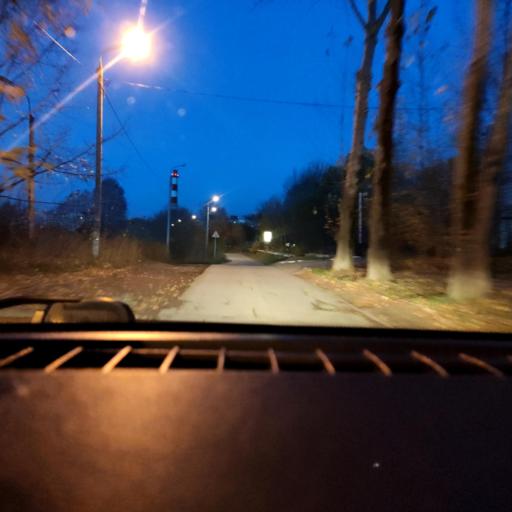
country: RU
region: Perm
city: Perm
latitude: 58.0598
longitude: 56.3578
